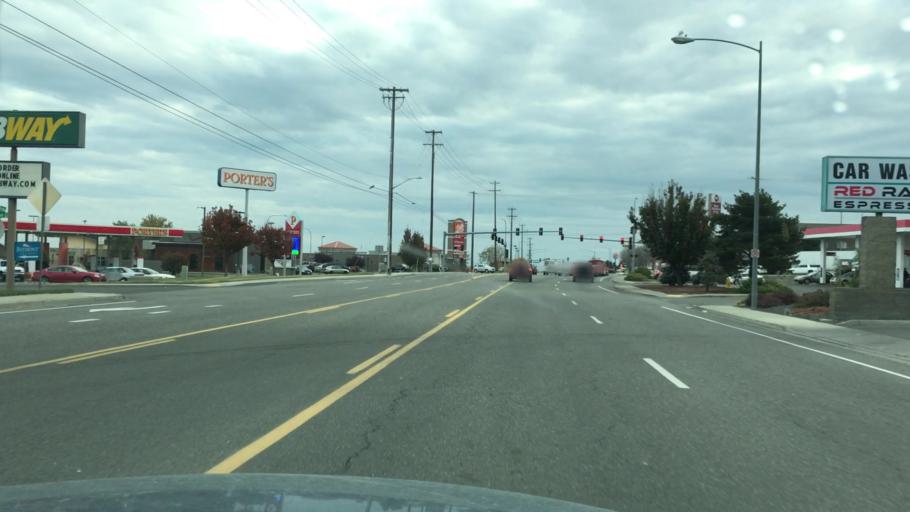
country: US
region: Washington
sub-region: Benton County
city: Kennewick
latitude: 46.1849
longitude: -119.1788
